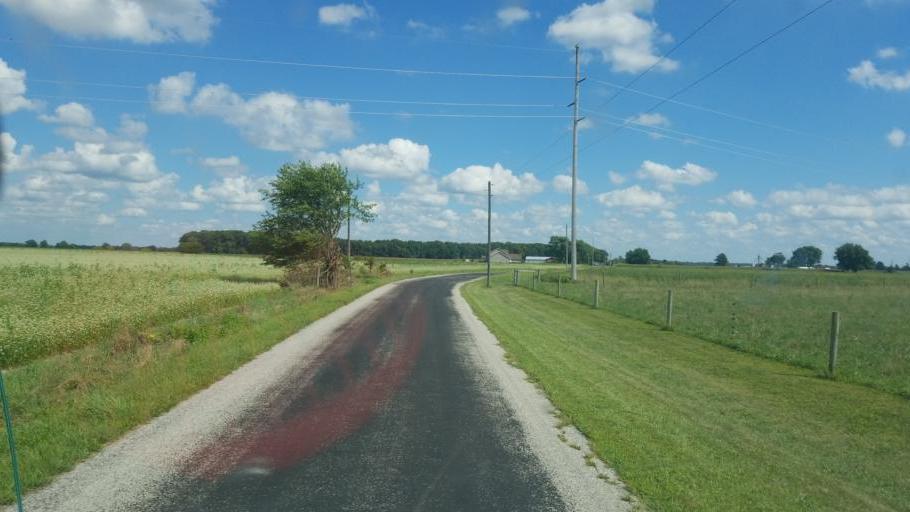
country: US
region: Ohio
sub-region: Marion County
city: Prospect
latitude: 40.3651
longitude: -83.2176
